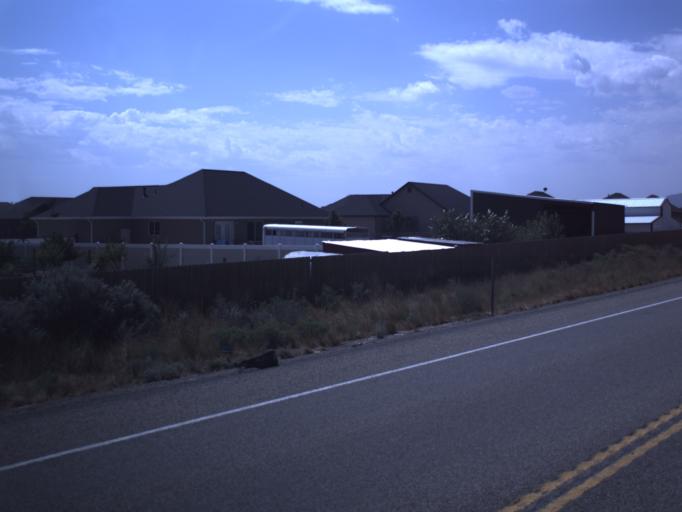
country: US
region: Utah
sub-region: Utah County
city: Eagle Mountain
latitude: 40.3757
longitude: -112.0125
